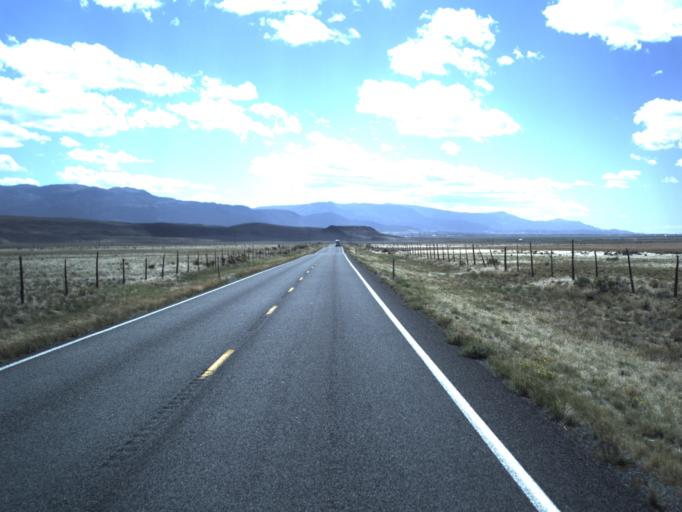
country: US
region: Utah
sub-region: Iron County
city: Enoch
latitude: 37.8971
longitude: -113.0316
